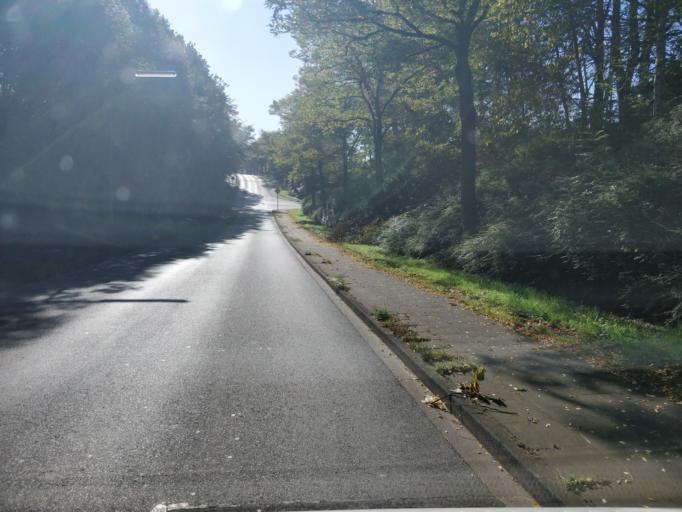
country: DE
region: North Rhine-Westphalia
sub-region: Regierungsbezirk Koln
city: Sinnersdorf
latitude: 51.0500
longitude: 6.8537
